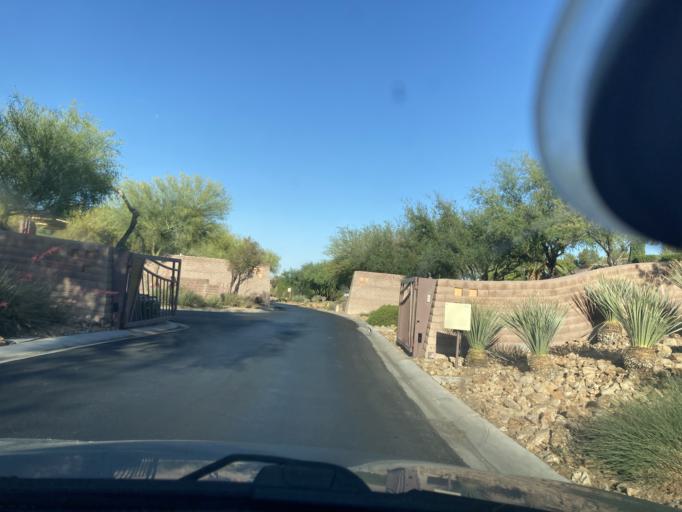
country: US
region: Nevada
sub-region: Clark County
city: Summerlin South
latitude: 36.1257
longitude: -115.3421
